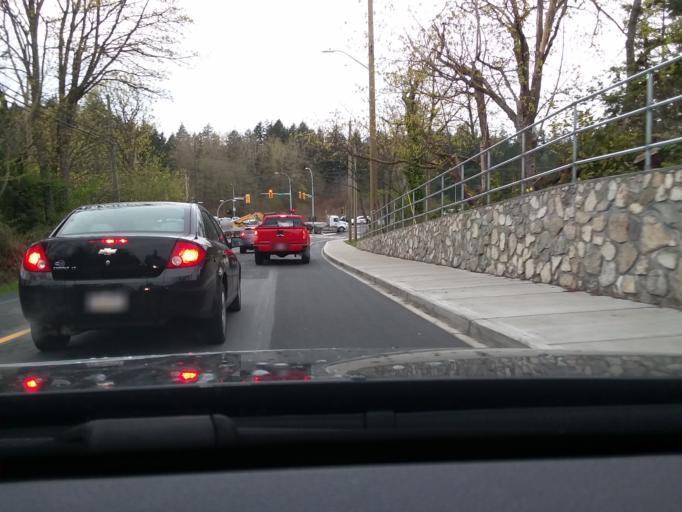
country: CA
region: British Columbia
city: Victoria
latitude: 48.5143
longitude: -123.3828
